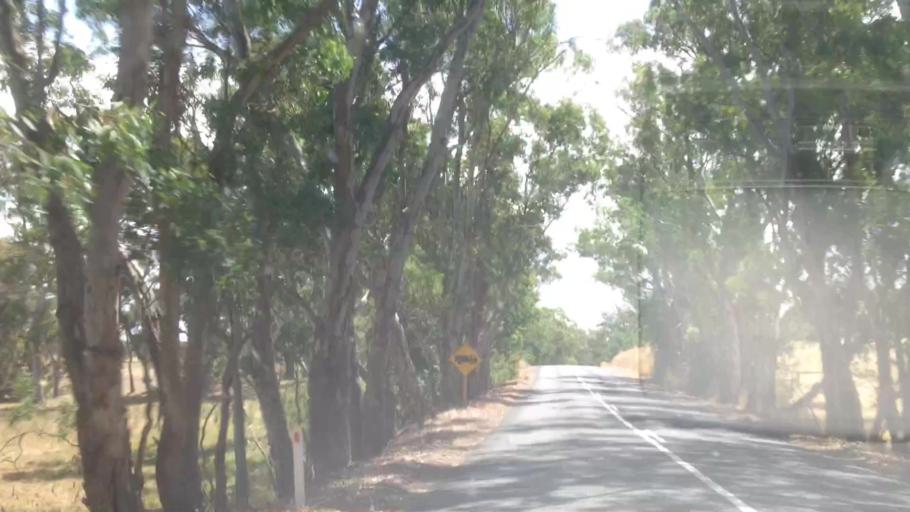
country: AU
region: South Australia
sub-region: Adelaide Hills
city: Birdwood
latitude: -34.7911
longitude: 138.9614
